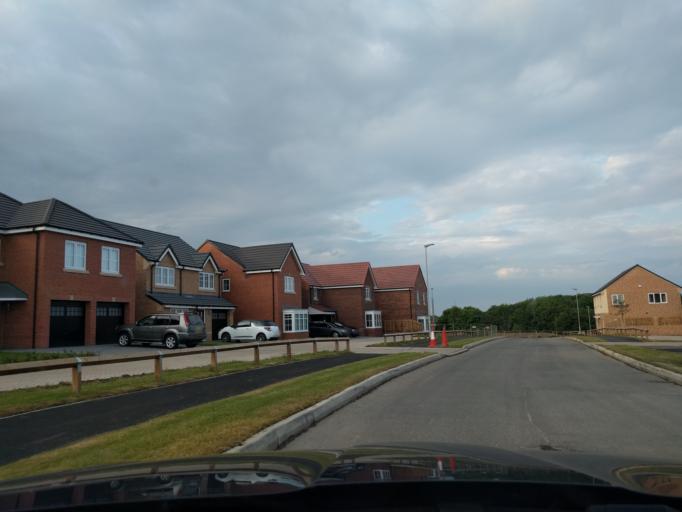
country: GB
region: England
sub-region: Northumberland
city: Choppington
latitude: 55.1340
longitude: -1.6178
